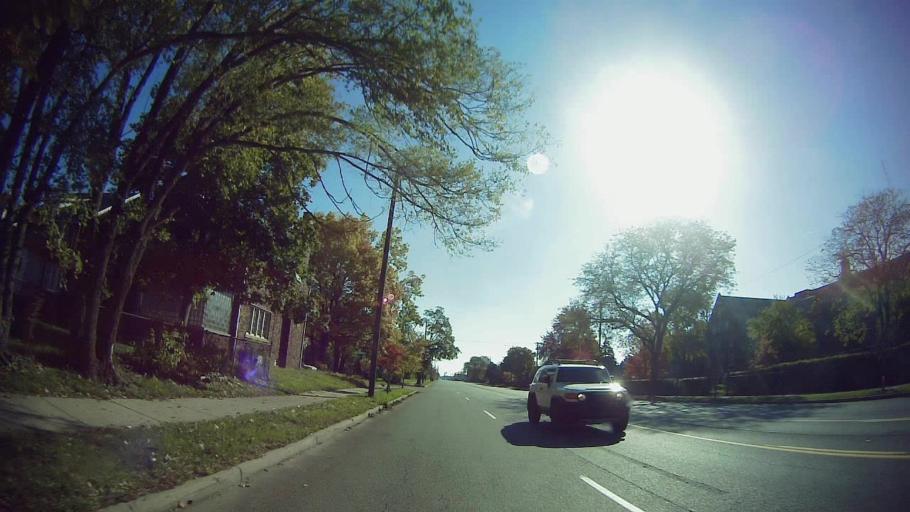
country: US
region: Michigan
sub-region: Wayne County
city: Highland Park
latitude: 42.3760
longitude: -83.1104
